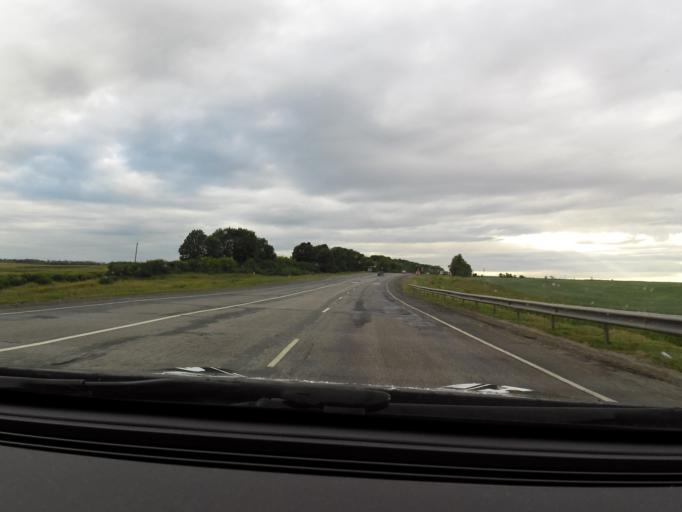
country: RU
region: Chuvashia
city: Tsivil'sk
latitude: 55.7905
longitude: 47.6777
